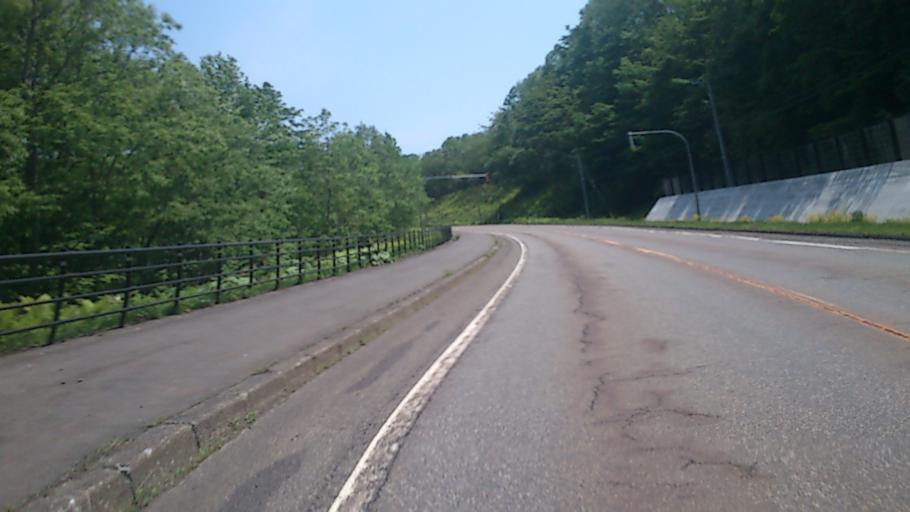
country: JP
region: Hokkaido
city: Otofuke
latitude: 43.3619
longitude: 143.2465
